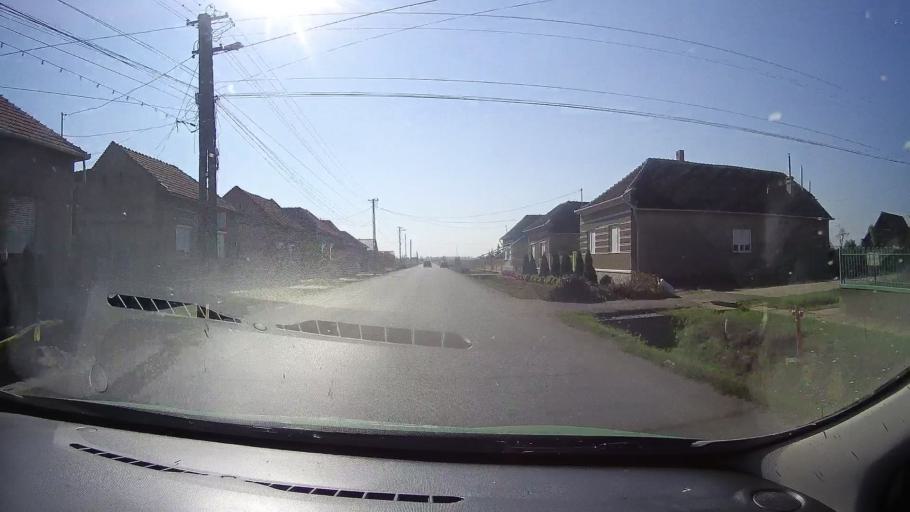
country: RO
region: Satu Mare
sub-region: Comuna Camin
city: Camin
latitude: 47.7239
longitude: 22.4759
